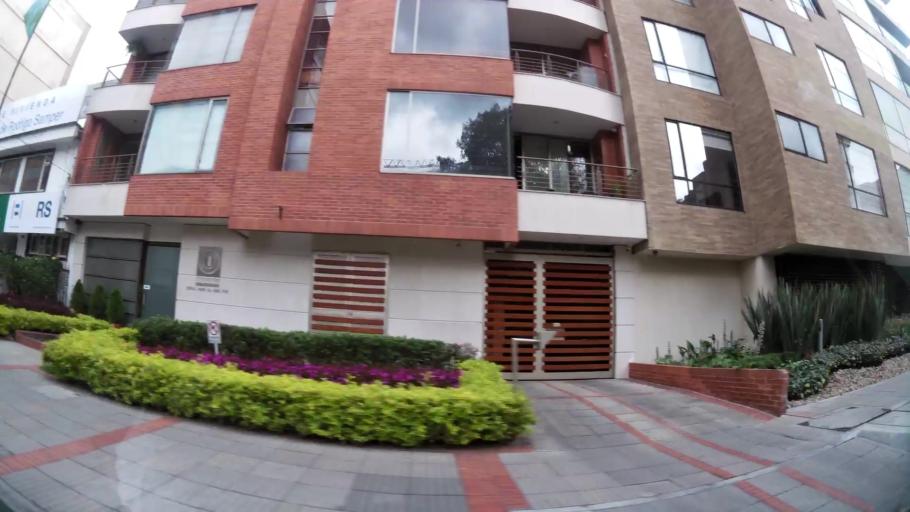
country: CO
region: Bogota D.C.
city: Barrio San Luis
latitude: 4.6728
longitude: -74.0579
